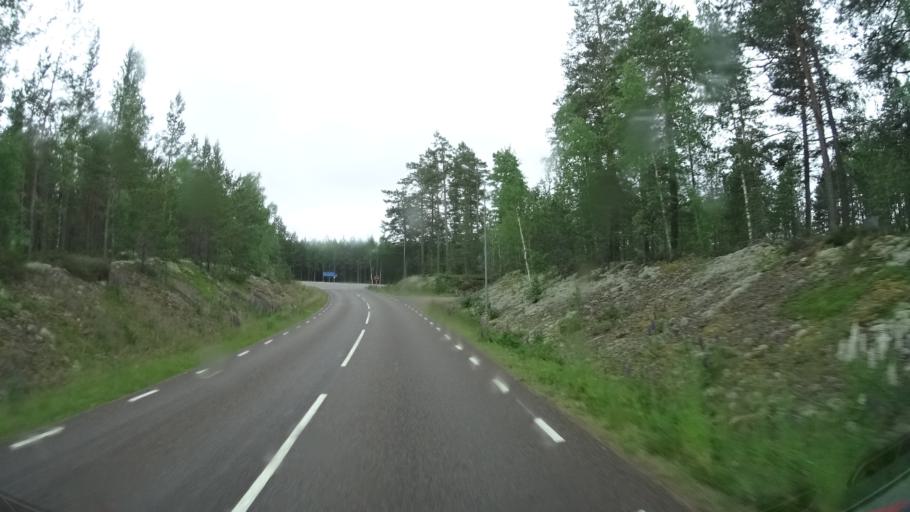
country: SE
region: Joenkoeping
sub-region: Eksjo Kommun
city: Mariannelund
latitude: 57.6251
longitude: 15.6008
